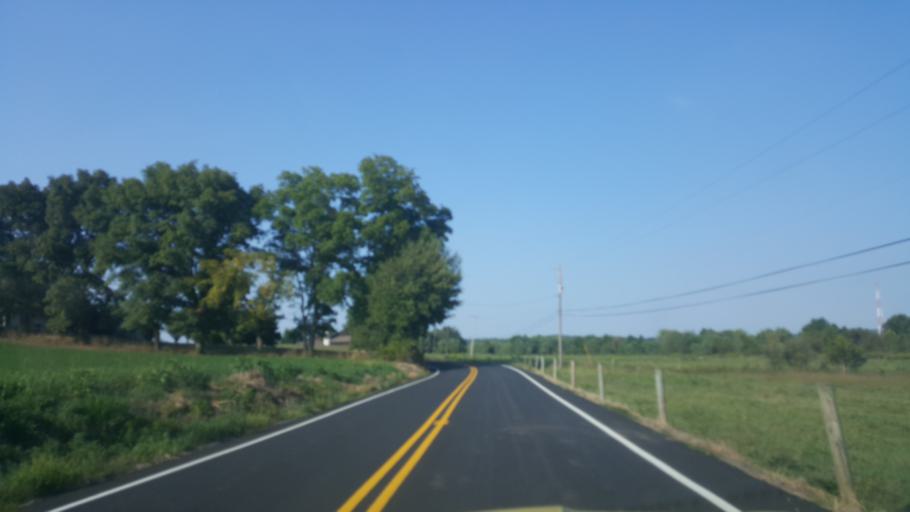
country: US
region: Pennsylvania
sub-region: Lebanon County
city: Campbelltown
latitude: 40.2205
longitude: -76.5575
